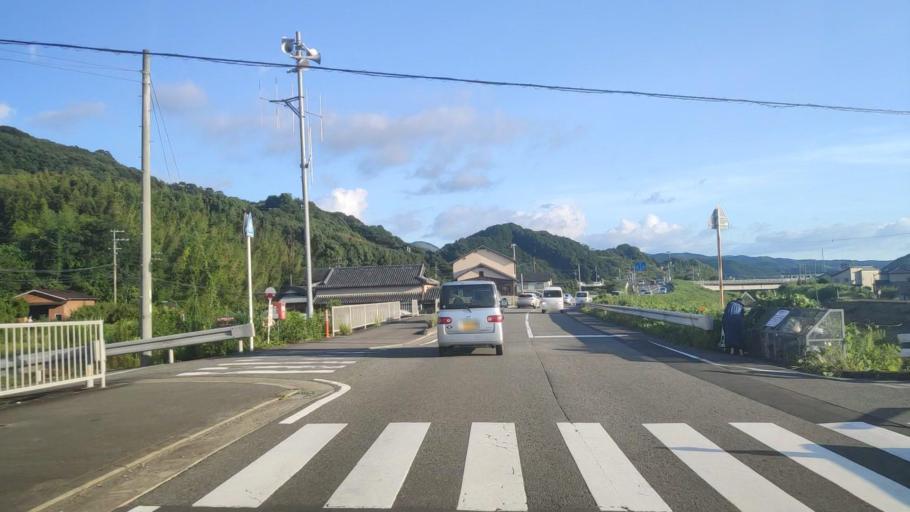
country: JP
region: Wakayama
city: Tanabe
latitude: 33.7156
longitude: 135.4478
